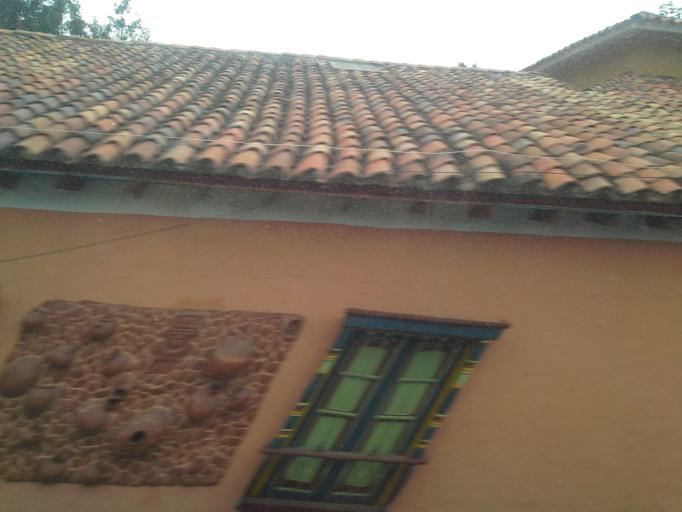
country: CO
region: Boyaca
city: Raquira
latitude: 5.5478
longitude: -73.6373
